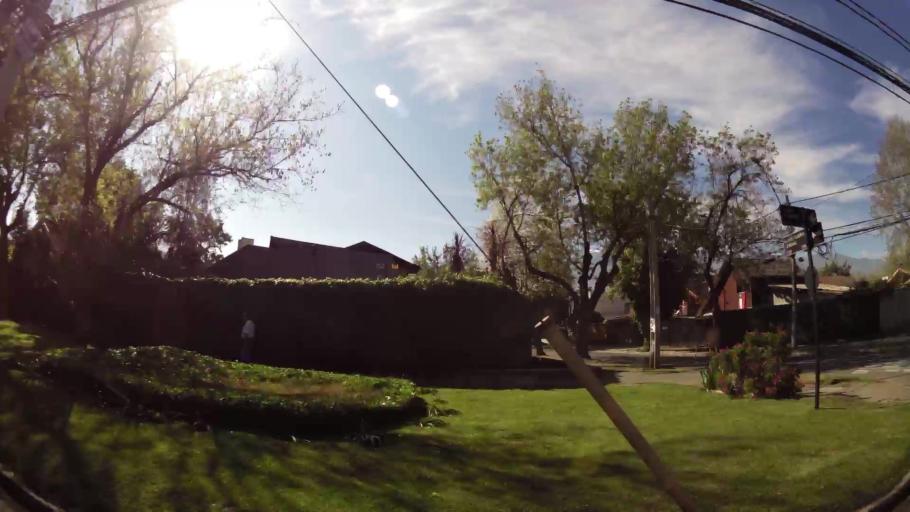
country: CL
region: Santiago Metropolitan
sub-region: Provincia de Santiago
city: Villa Presidente Frei, Nunoa, Santiago, Chile
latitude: -33.4324
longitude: -70.5574
